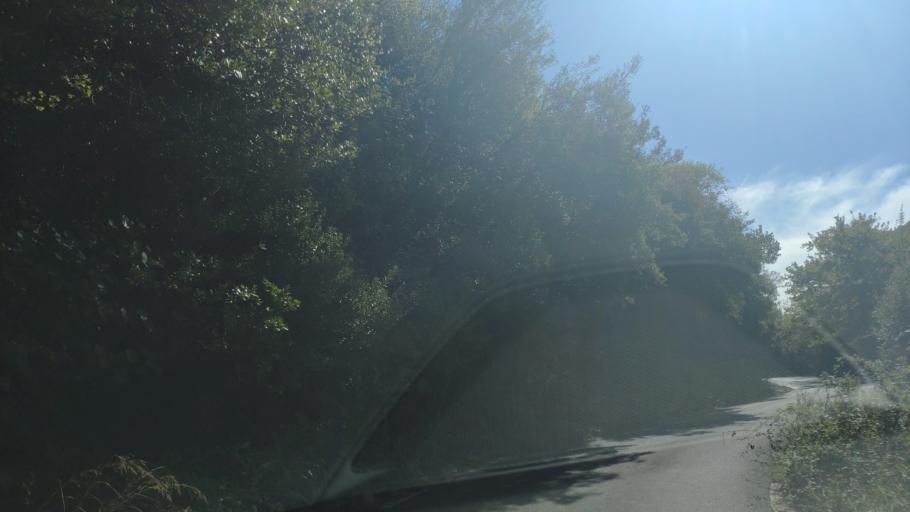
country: GR
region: Peloponnese
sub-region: Nomos Arkadias
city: Dimitsana
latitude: 37.5389
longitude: 22.0467
